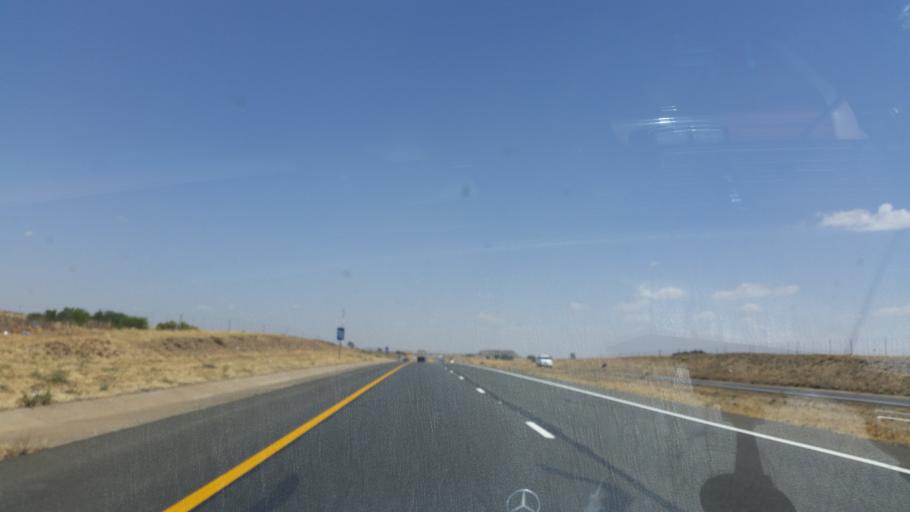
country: ZA
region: Orange Free State
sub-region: Lejweleputswa District Municipality
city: Brandfort
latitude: -28.9284
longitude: 26.4294
